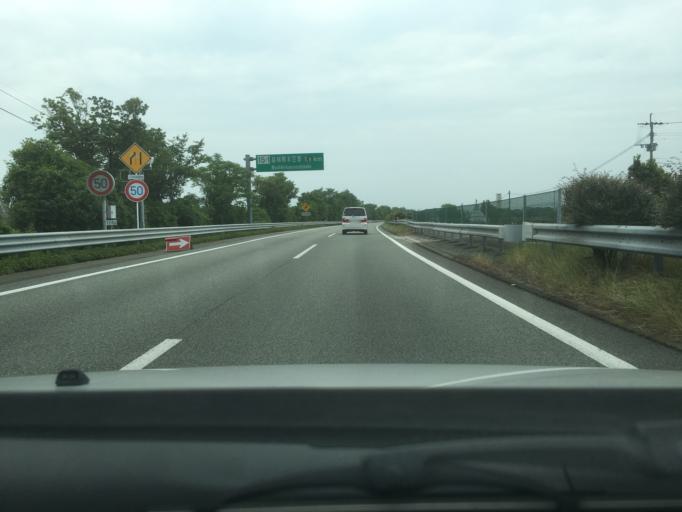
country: JP
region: Kumamoto
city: Ozu
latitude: 32.8057
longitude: 130.7935
